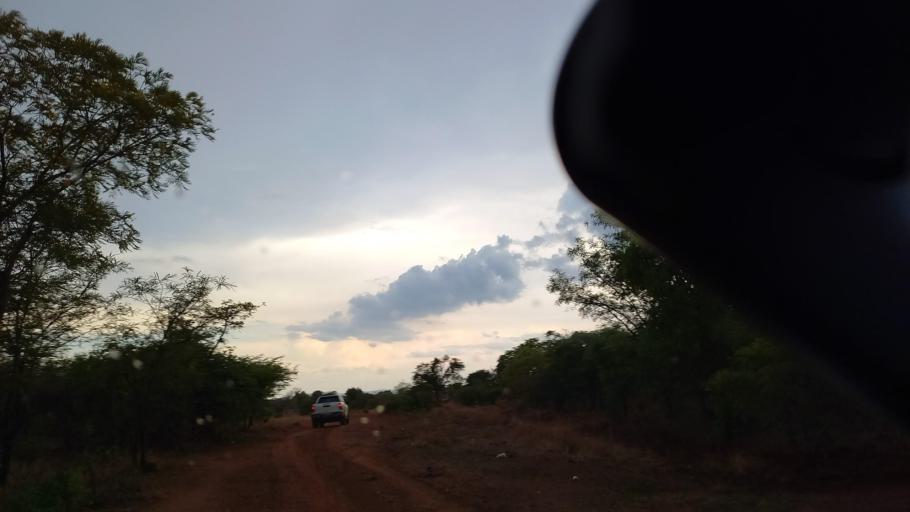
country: ZM
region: Lusaka
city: Kafue
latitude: -15.9781
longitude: 28.2555
